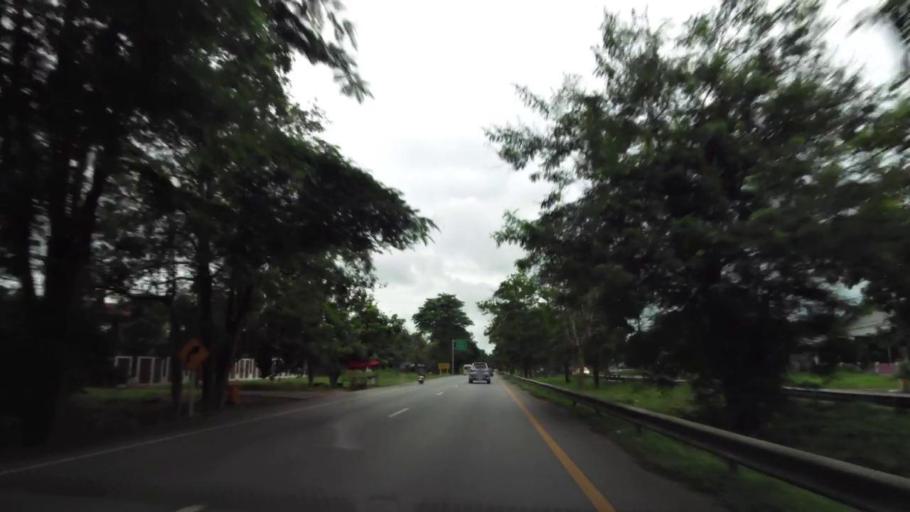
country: TH
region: Chanthaburi
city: Tha Mai
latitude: 12.6486
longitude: 102.0256
